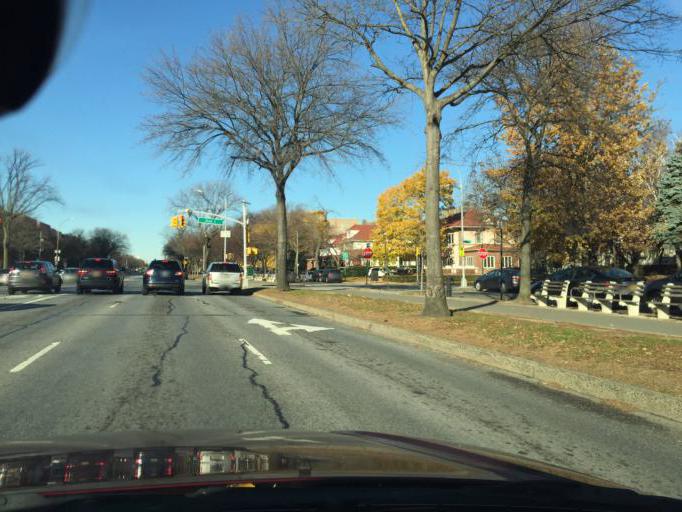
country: US
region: New York
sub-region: Kings County
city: Brooklyn
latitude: 40.6260
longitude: -73.9708
